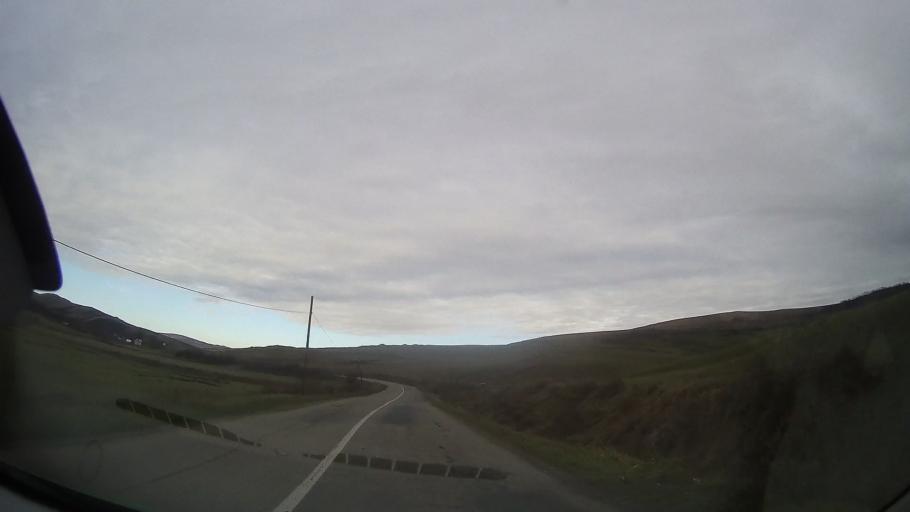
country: RO
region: Cluj
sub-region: Comuna Camarasu
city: Camarasu
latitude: 46.8098
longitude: 24.1436
